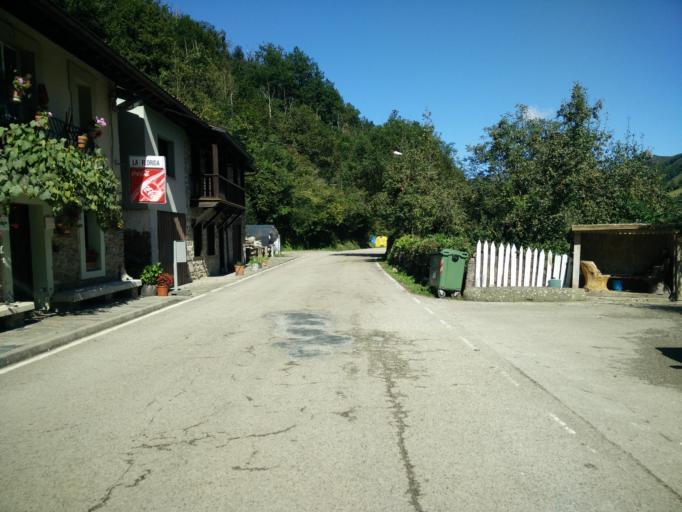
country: ES
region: Cantabria
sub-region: Provincia de Cantabria
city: Ruente
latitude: 43.1423
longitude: -4.2886
